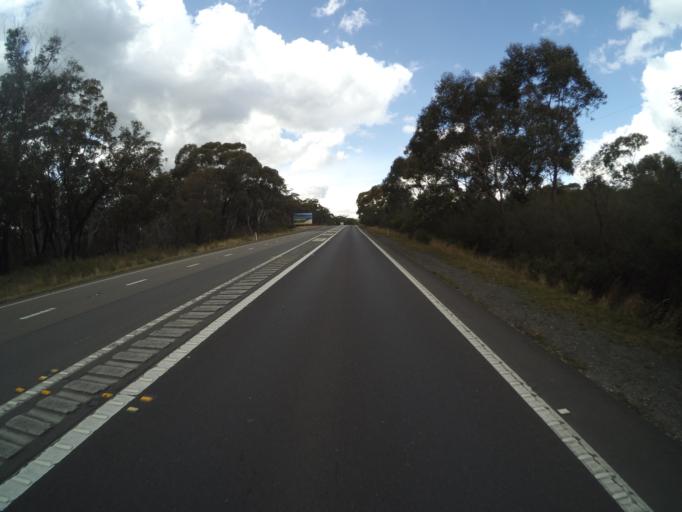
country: AU
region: New South Wales
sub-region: Wollondilly
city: Douglas Park
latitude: -34.3180
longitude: 150.7540
